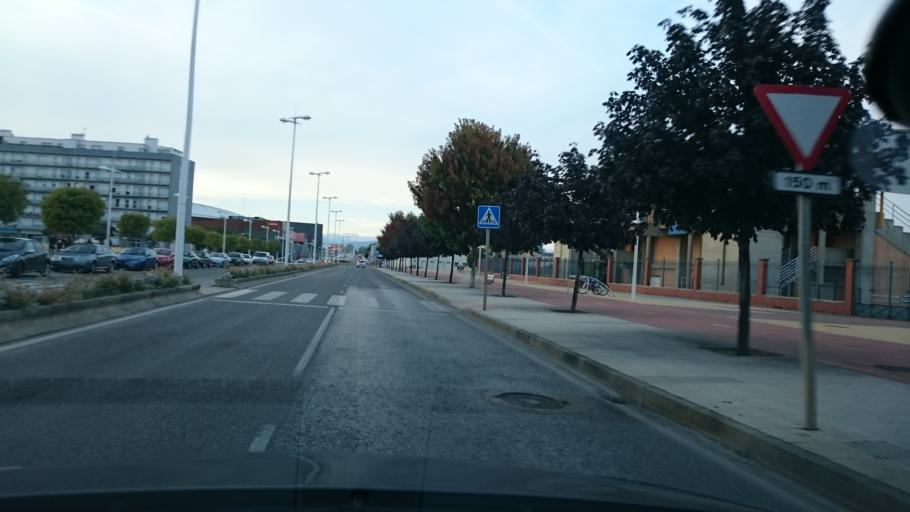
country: ES
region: Castille and Leon
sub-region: Provincia de Leon
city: Ponferrada
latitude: 42.5542
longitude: -6.6007
